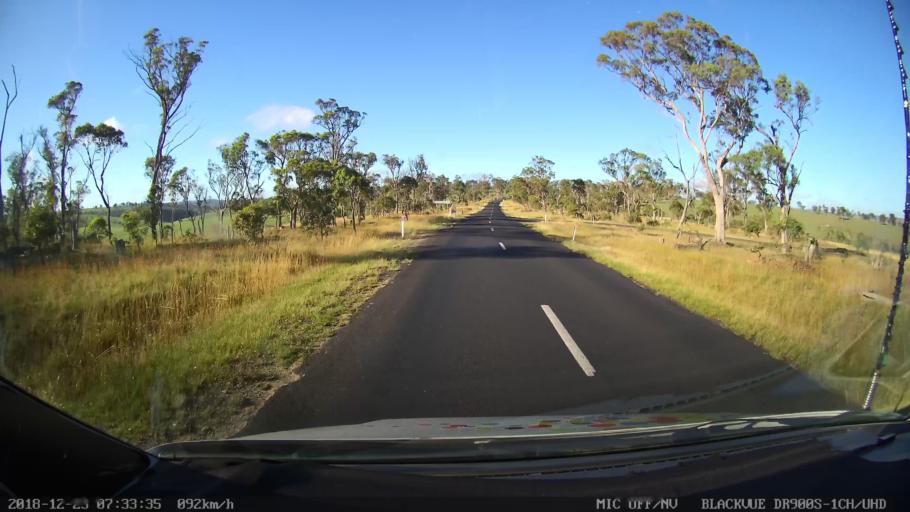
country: AU
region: New South Wales
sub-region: Armidale Dumaresq
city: Enmore
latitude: -30.5138
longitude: 152.1030
